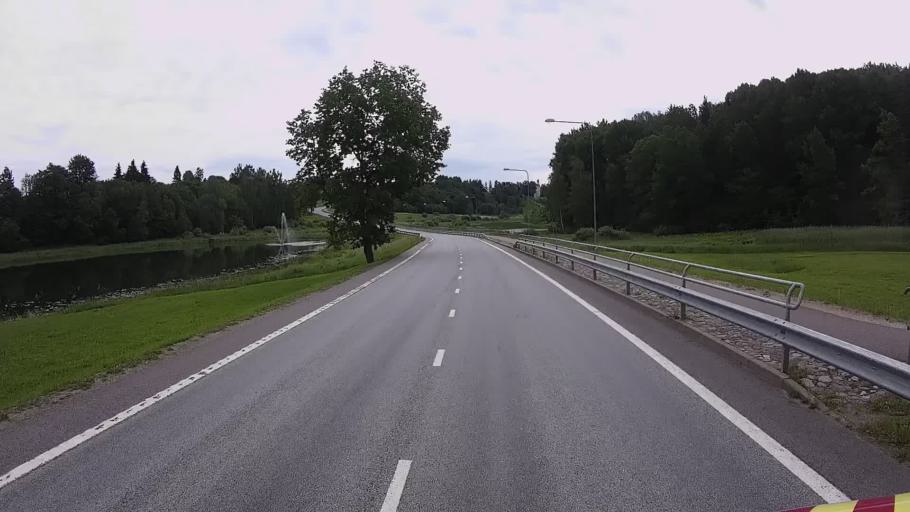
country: EE
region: Viljandimaa
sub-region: Karksi vald
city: Karksi-Nuia
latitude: 58.1076
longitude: 25.5516
